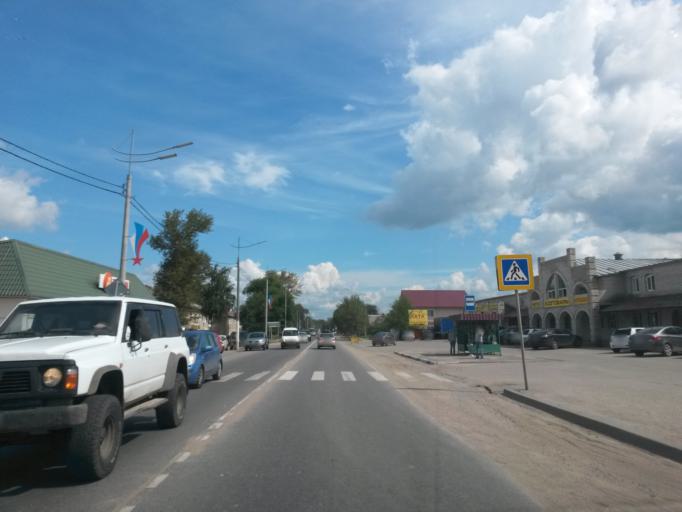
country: RU
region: Jaroslavl
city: Pereslavl'-Zalesskiy
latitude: 56.7216
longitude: 38.8319
